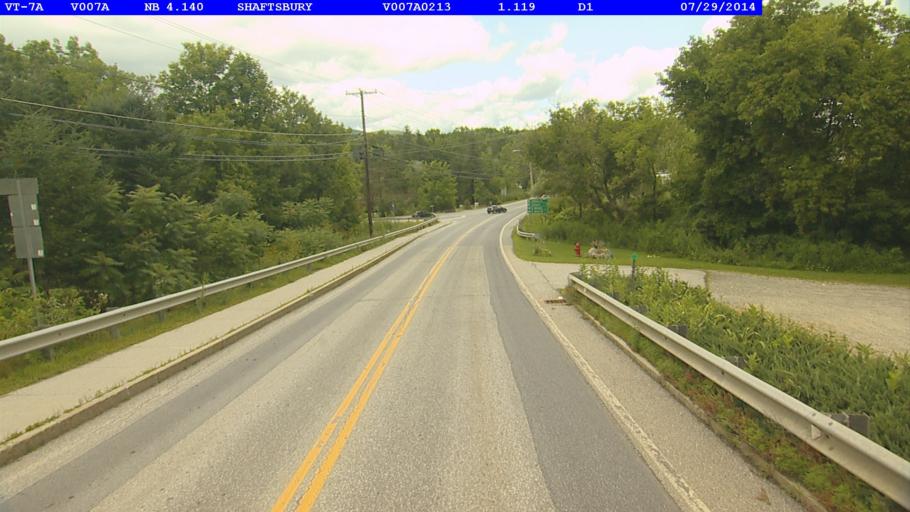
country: US
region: Vermont
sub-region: Bennington County
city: North Bennington
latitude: 42.9487
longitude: -73.2114
